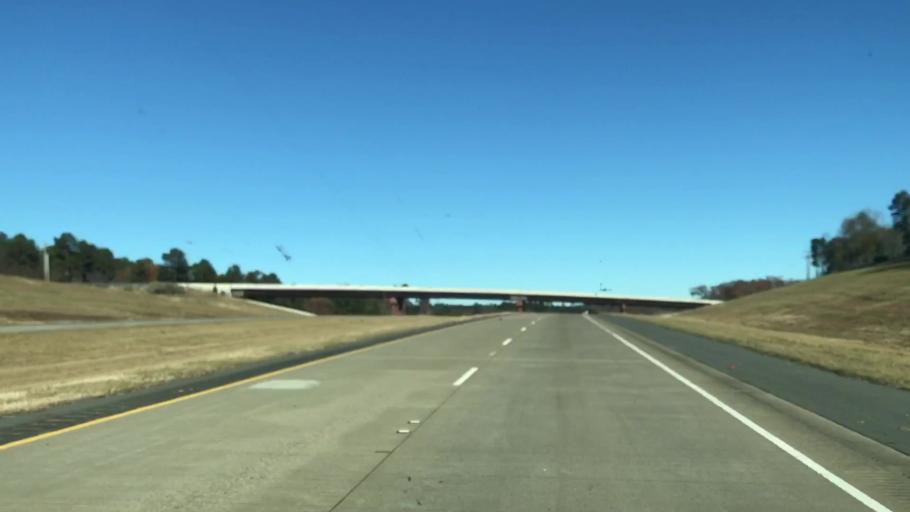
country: US
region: Louisiana
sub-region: Caddo Parish
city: Vivian
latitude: 32.9760
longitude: -93.9089
